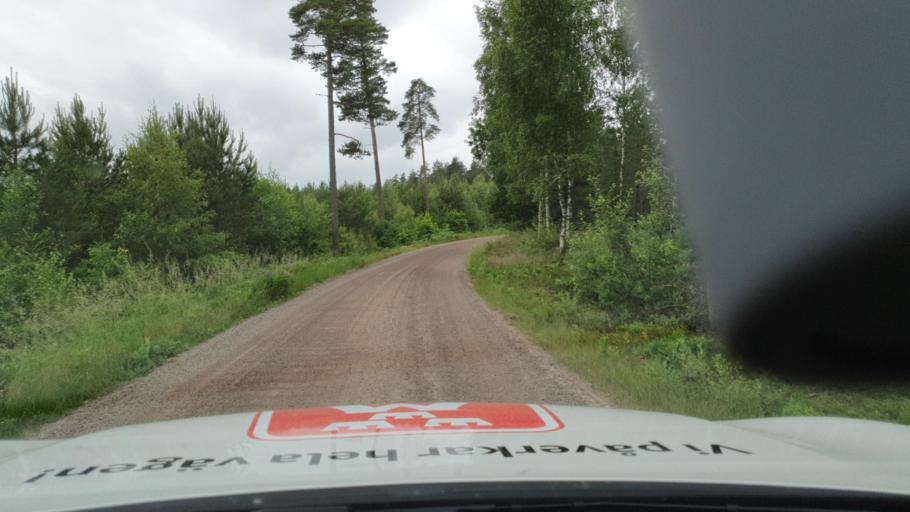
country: SE
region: Vaestra Goetaland
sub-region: Hjo Kommun
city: Hjo
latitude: 58.3406
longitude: 14.2849
